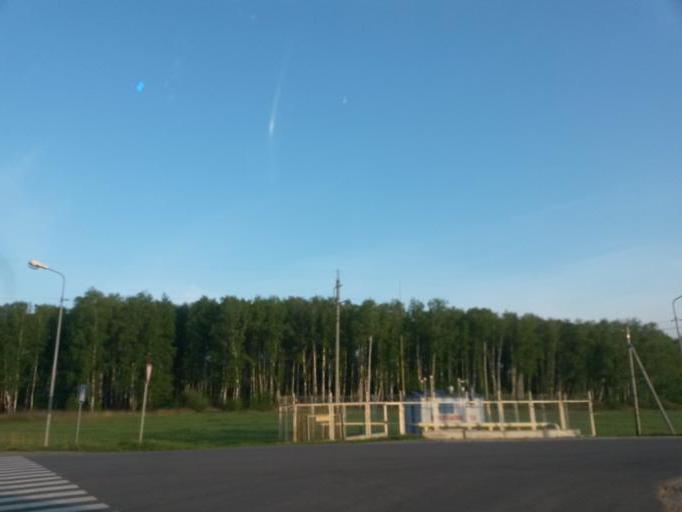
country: RU
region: Moskovskaya
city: Lyubuchany
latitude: 55.2456
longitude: 37.5319
